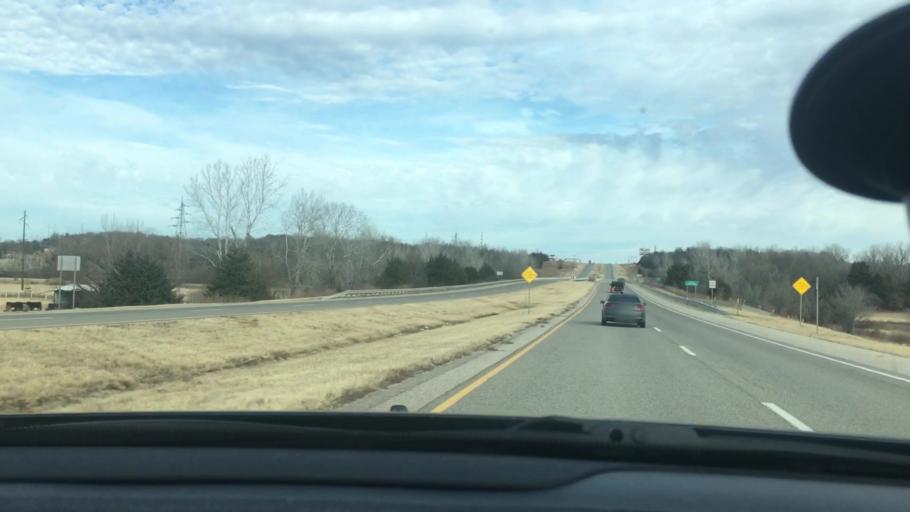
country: US
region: Oklahoma
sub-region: Pontotoc County
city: Byng
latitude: 34.9285
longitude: -96.6838
